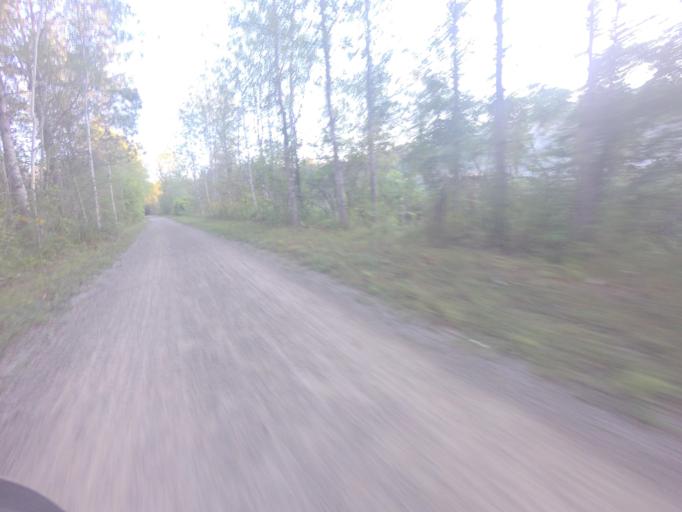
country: CA
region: Ontario
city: Bradford West Gwillimbury
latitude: 43.9976
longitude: -79.8040
